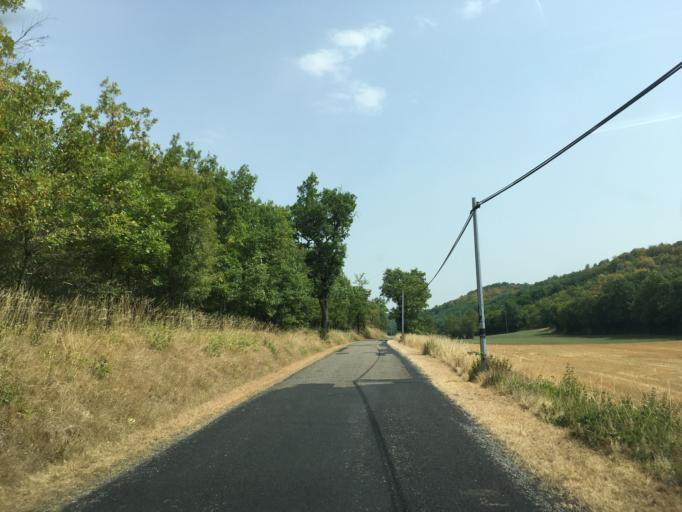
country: FR
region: Midi-Pyrenees
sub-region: Departement du Lot
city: Le Vigan
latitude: 44.7460
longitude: 1.5238
